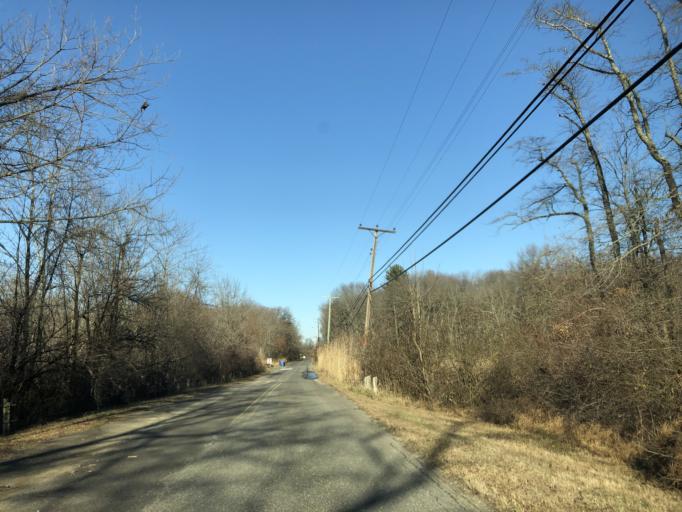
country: US
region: Pennsylvania
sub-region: Delaware County
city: Chester
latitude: 39.8043
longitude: -75.3549
